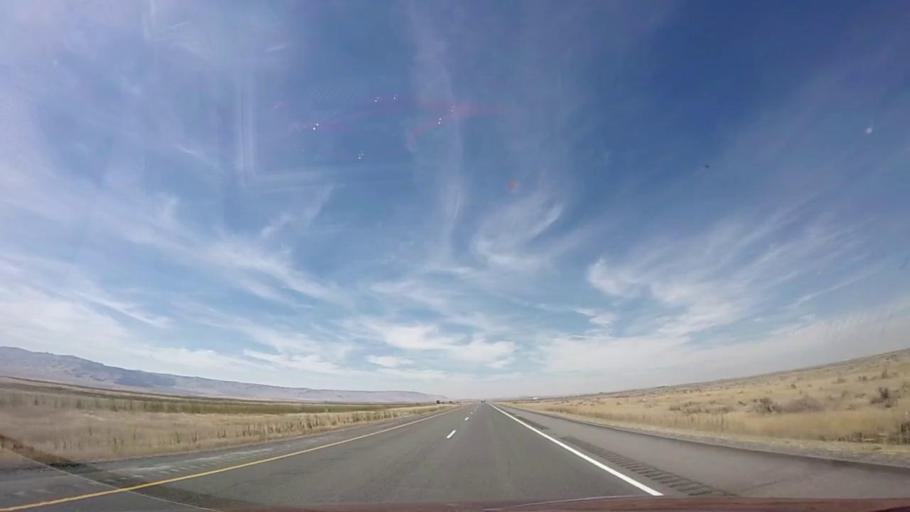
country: US
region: Idaho
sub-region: Minidoka County
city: Rupert
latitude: 42.3703
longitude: -113.2663
